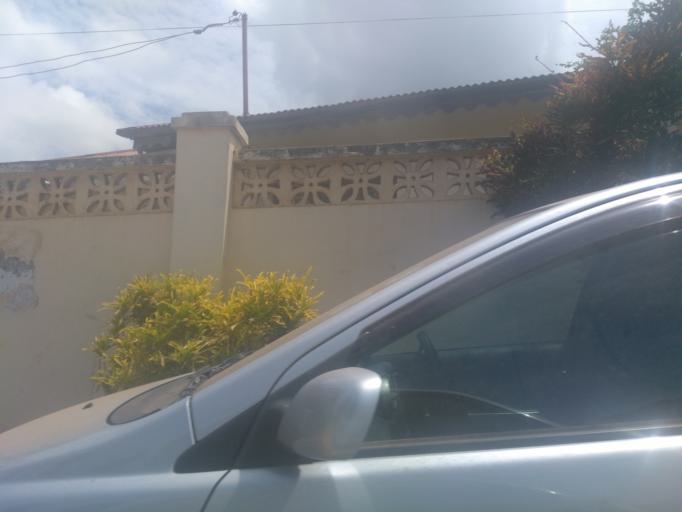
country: TZ
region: Zanzibar Urban/West
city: Zanzibar
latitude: -6.2312
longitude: 39.2190
